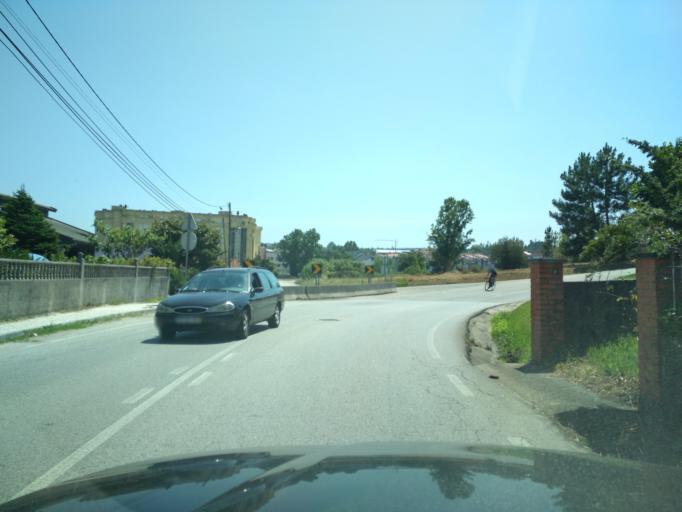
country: PT
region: Coimbra
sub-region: Condeixa-A-Nova
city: Condeixa-a-Nova
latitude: 40.1096
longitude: -8.5057
